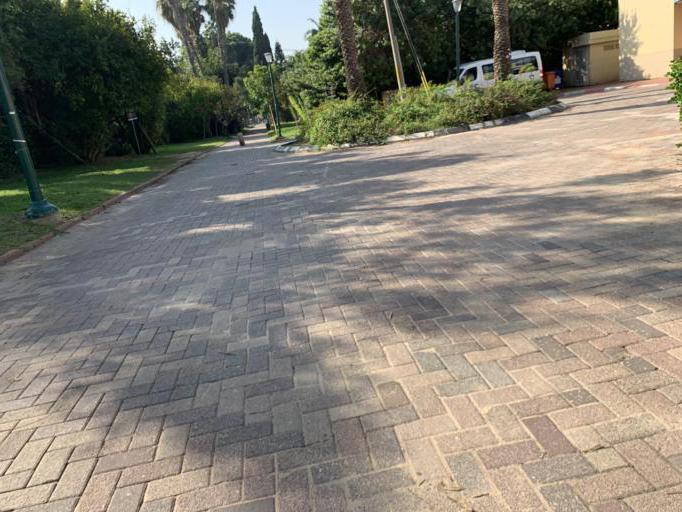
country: IL
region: Tel Aviv
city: Ramat Gan
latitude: 32.0948
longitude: 34.8164
